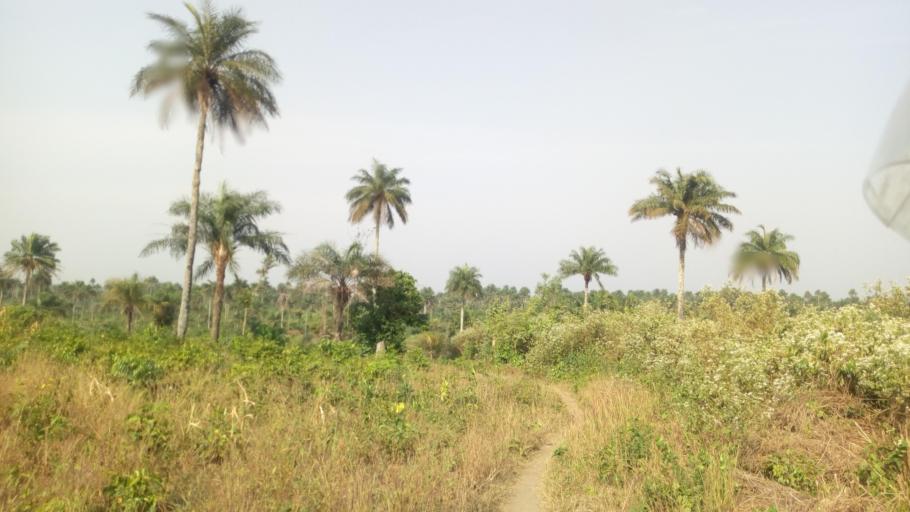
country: SL
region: Southern Province
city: Mogbwemo
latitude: 7.6159
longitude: -12.1725
